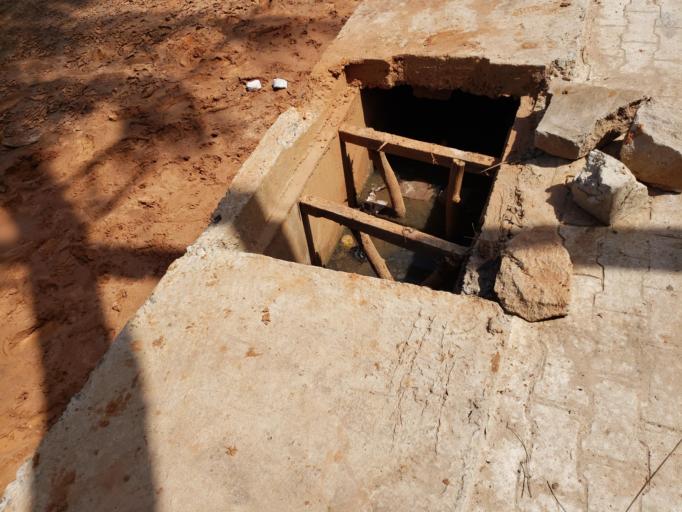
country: TG
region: Maritime
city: Lome
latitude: 6.1938
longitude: 1.1923
